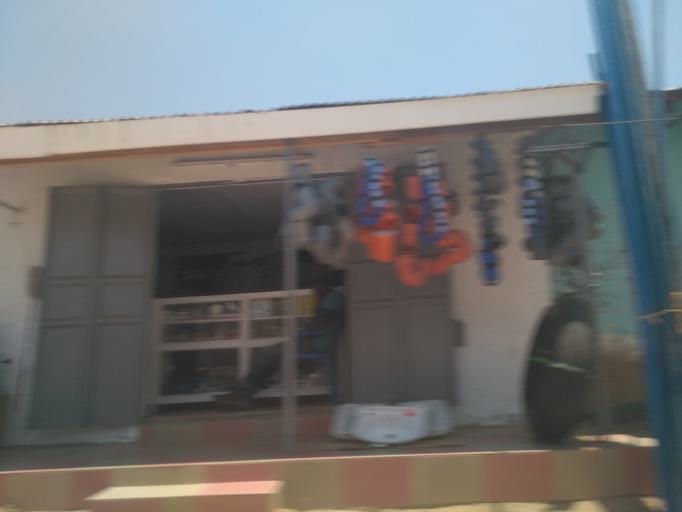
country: TZ
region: Dodoma
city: Dodoma
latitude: -6.1760
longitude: 35.7434
